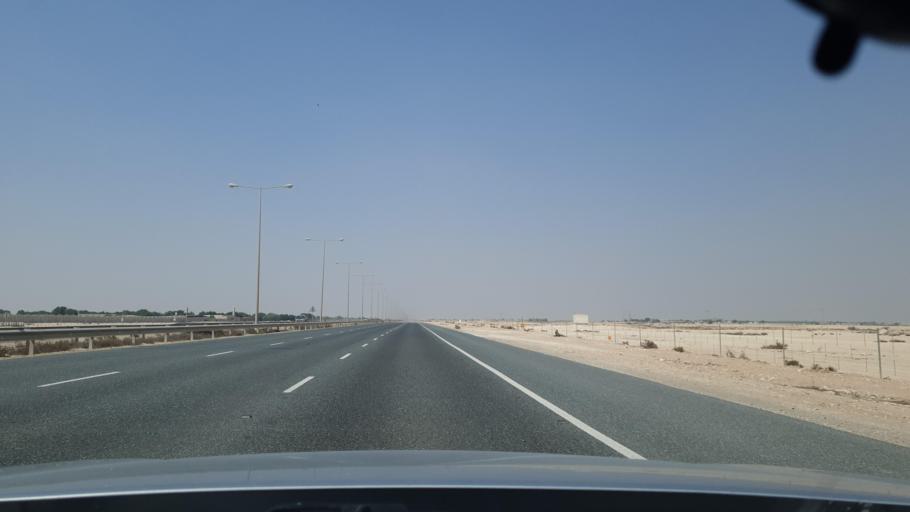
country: QA
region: Al Khawr
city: Al Khawr
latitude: 25.7599
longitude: 51.4249
